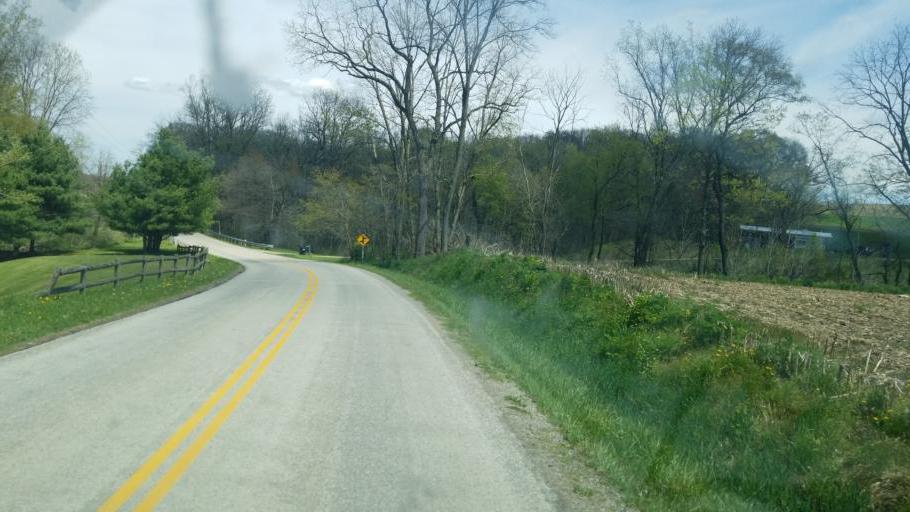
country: US
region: Ohio
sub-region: Ashland County
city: Loudonville
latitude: 40.7698
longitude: -82.2243
